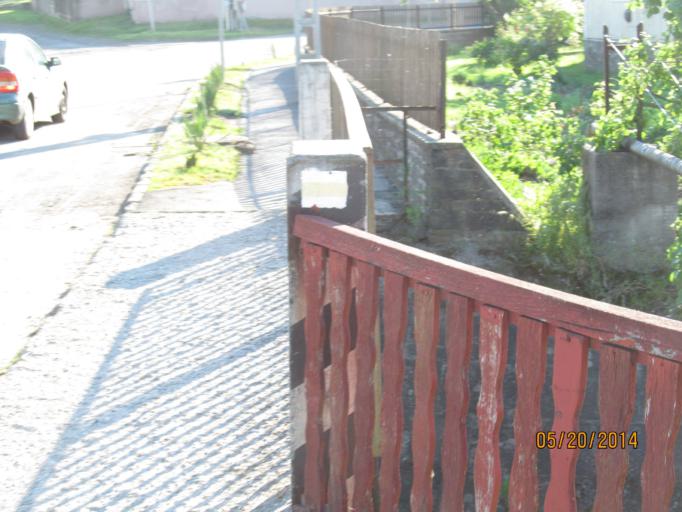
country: HU
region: Heves
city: Domoszlo
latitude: 47.8516
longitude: 20.1448
